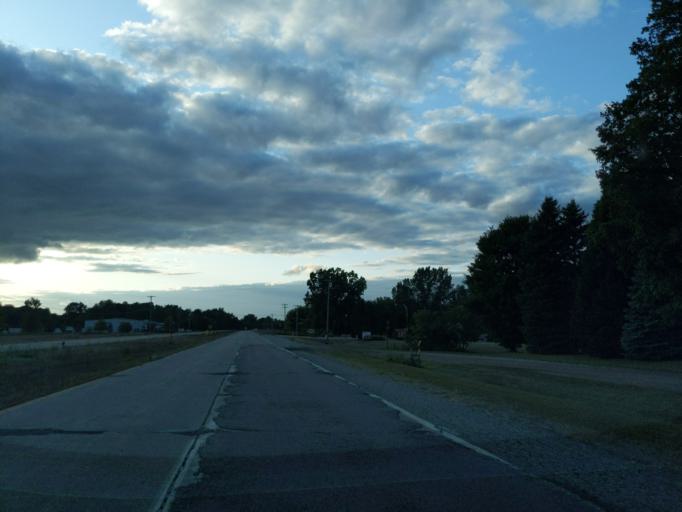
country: US
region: Michigan
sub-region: Ingham County
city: Holt
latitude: 42.6112
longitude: -84.4906
